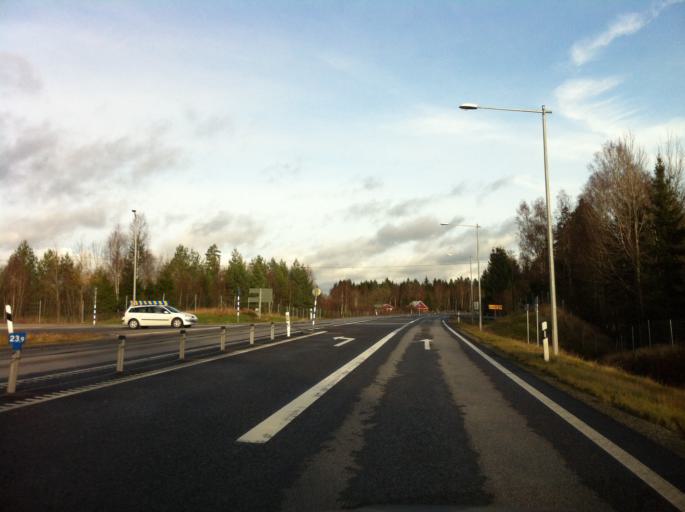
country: SE
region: Kronoberg
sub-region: Almhults Kommun
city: AElmhult
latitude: 56.6439
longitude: 14.2726
